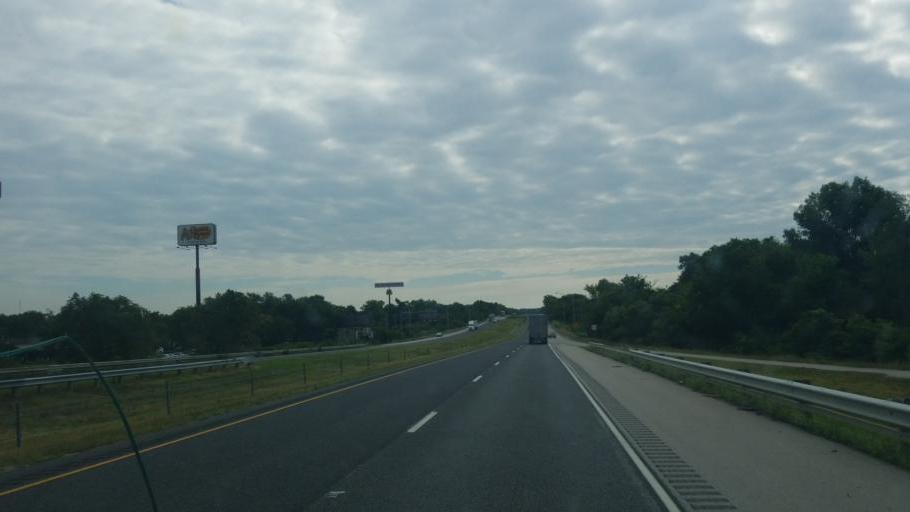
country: US
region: Indiana
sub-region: Vigo County
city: Terre Haute
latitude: 39.4306
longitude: -87.4127
